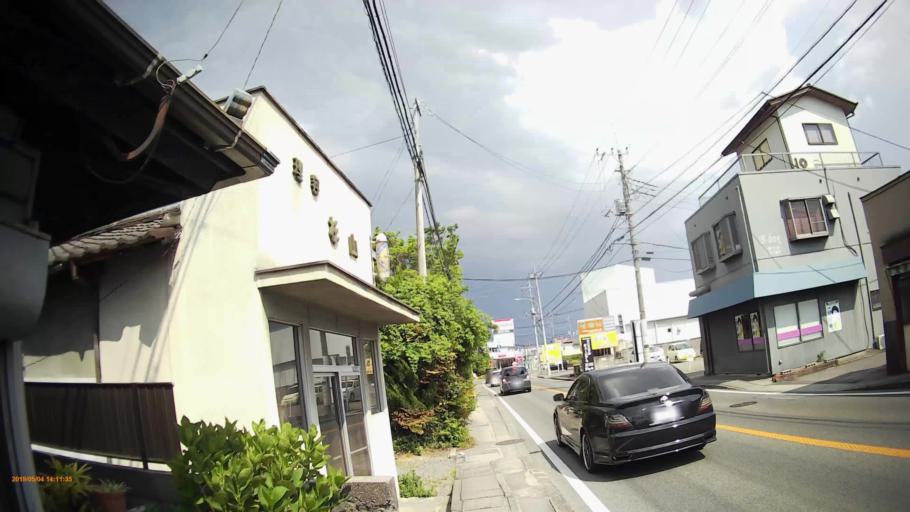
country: JP
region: Yamanashi
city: Kofu-shi
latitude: 35.6605
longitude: 138.5427
